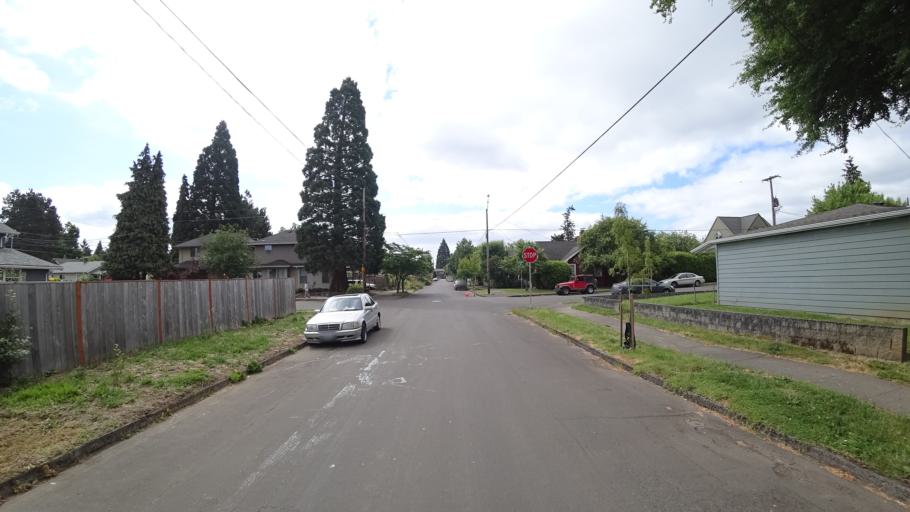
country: US
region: Oregon
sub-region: Washington County
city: West Haven
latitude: 45.5956
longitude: -122.7578
